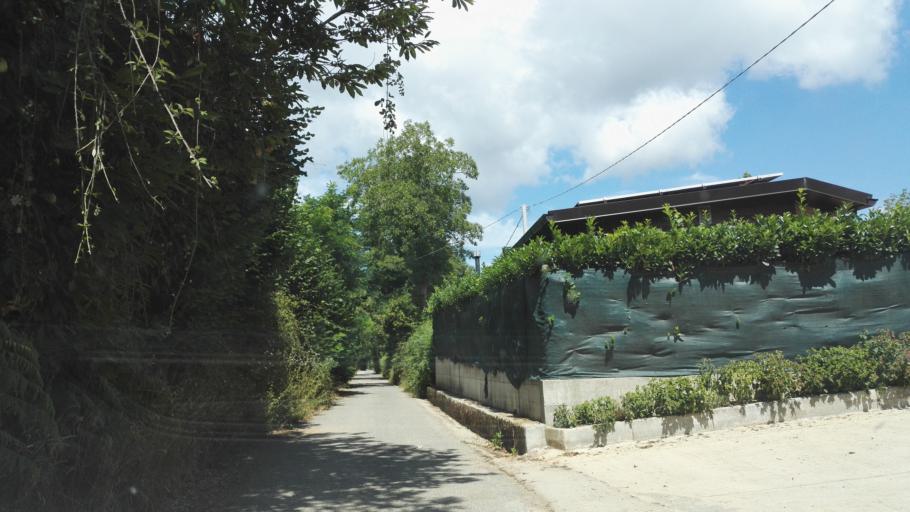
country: IT
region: Calabria
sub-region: Provincia di Vibo-Valentia
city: Serra San Bruno
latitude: 38.5605
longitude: 16.3310
